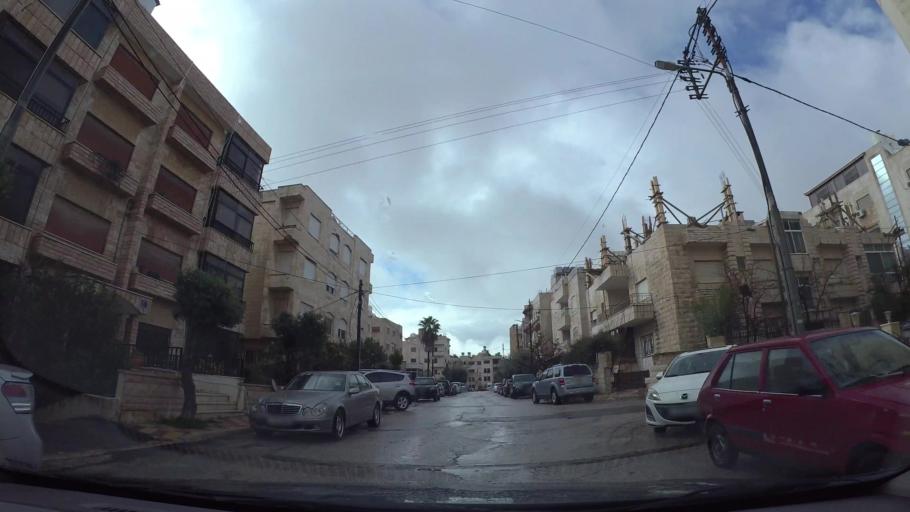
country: JO
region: Amman
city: Wadi as Sir
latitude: 31.9735
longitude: 35.8591
